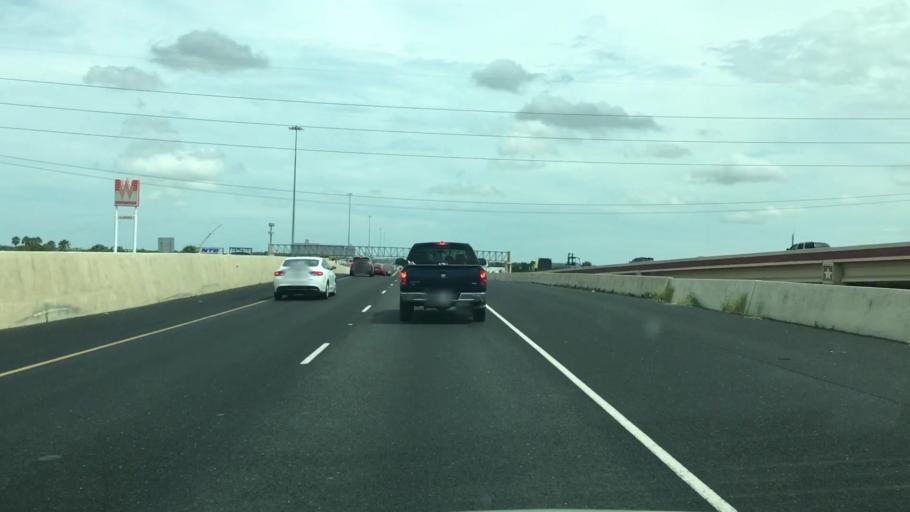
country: US
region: Texas
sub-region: Nueces County
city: Corpus Christi
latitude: 27.7359
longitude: -97.4283
